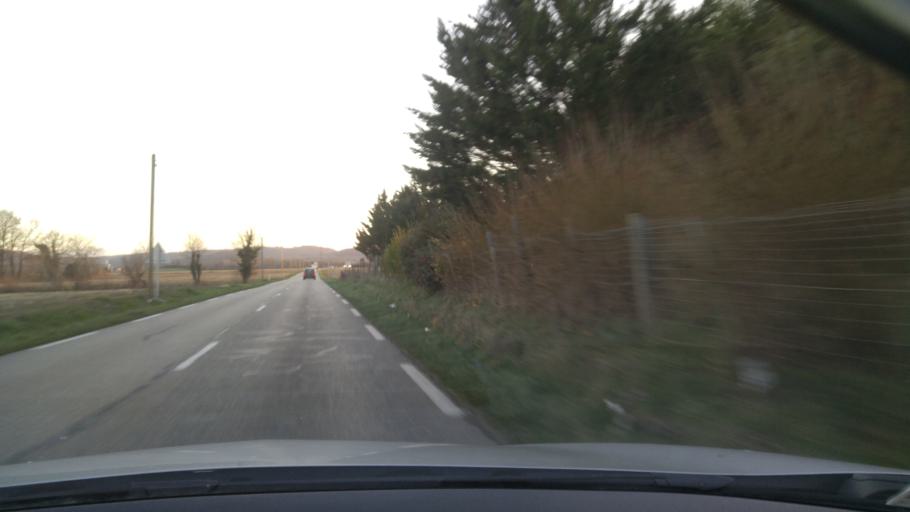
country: FR
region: Rhone-Alpes
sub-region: Departement de l'Isere
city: Tignieu-Jameyzieu
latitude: 45.7245
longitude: 5.1876
